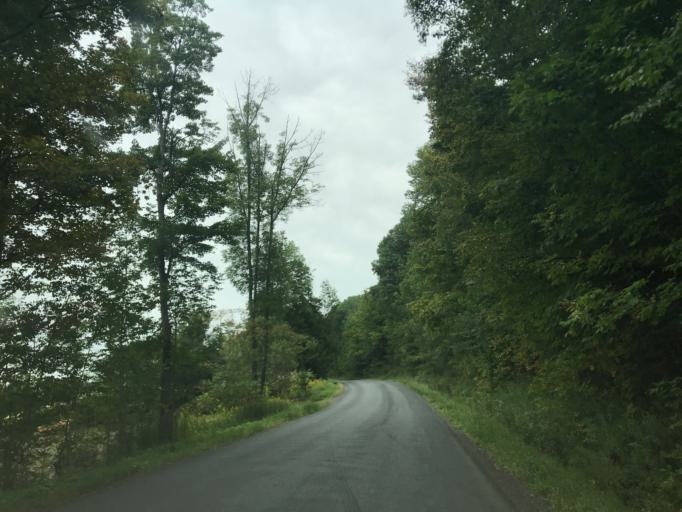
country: US
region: New York
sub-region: Otsego County
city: Worcester
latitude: 42.5896
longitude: -74.7137
